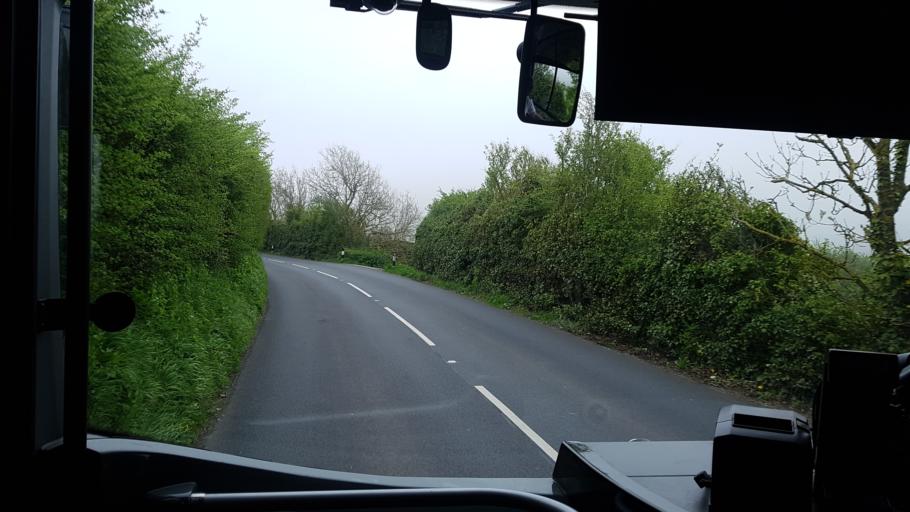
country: GB
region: England
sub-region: Isle of Wight
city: Ventnor
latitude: 50.6032
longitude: -1.2235
